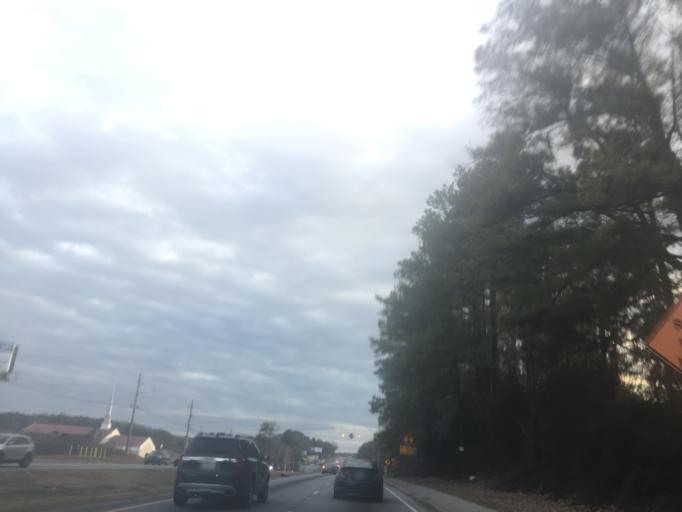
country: US
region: Georgia
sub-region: Clayton County
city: Riverdale
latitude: 33.5965
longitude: -84.4072
